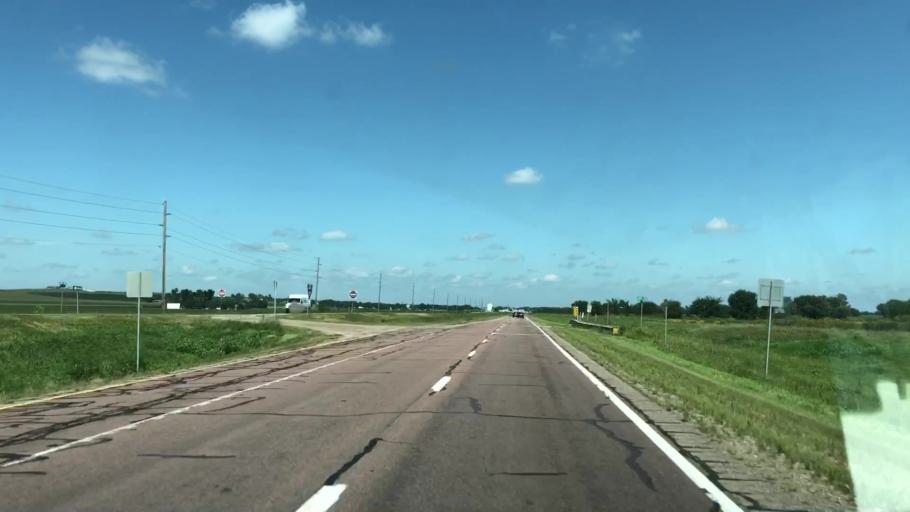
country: US
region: Iowa
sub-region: Plymouth County
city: Le Mars
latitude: 42.6916
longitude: -96.2624
